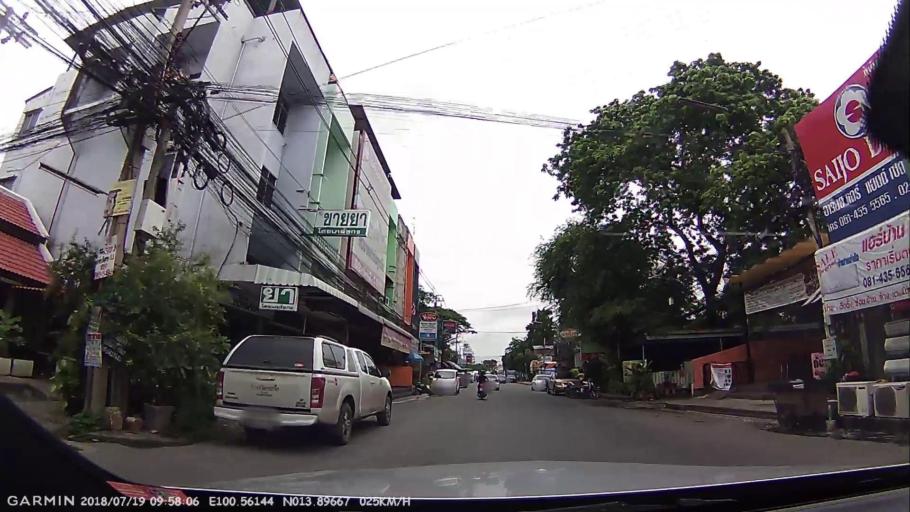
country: TH
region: Bangkok
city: Lak Si
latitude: 13.8967
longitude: 100.5615
